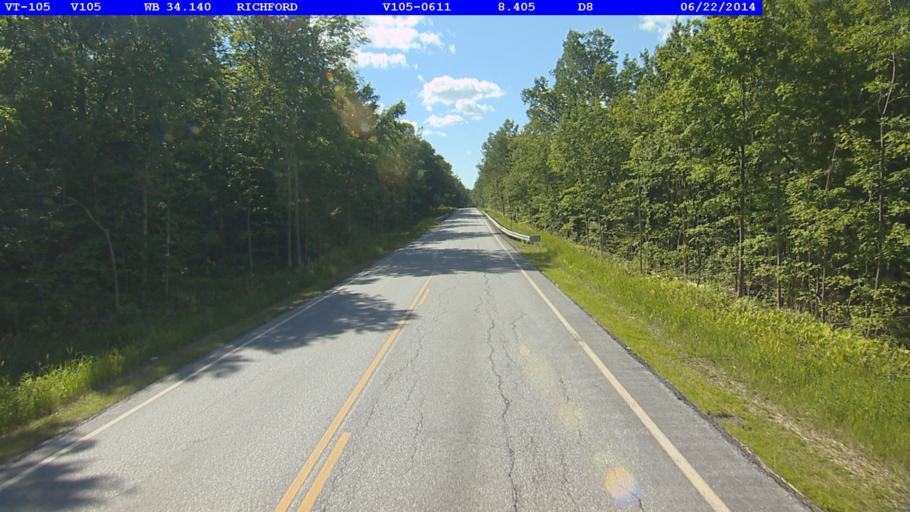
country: US
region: Vermont
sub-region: Franklin County
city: Richford
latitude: 44.9919
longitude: -72.5638
